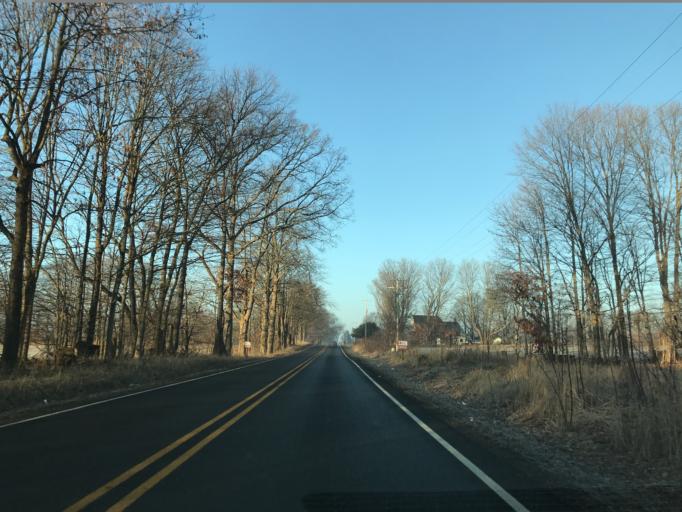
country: US
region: Michigan
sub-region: Ingham County
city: Leslie
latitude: 42.3787
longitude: -84.4339
